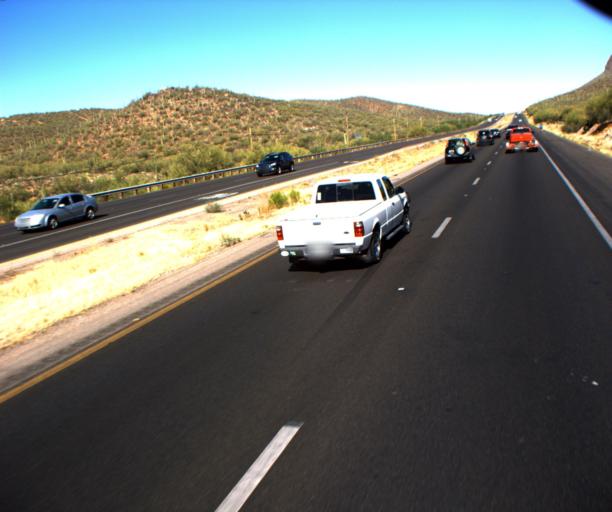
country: US
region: Arizona
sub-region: Pima County
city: Drexel Heights
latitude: 32.1768
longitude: -111.0289
